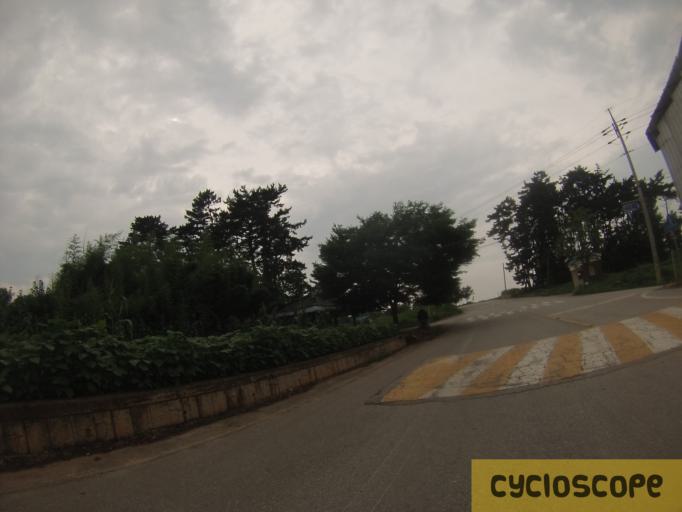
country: KR
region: Jeollabuk-do
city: Kimje
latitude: 35.8518
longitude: 126.8154
